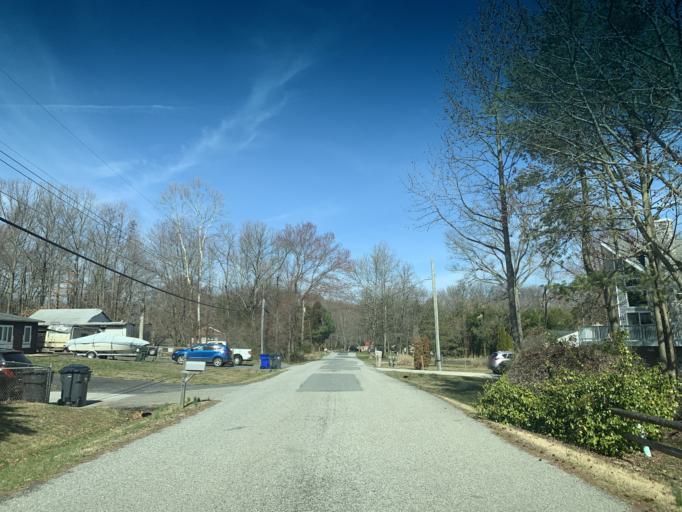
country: US
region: Maryland
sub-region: Cecil County
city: Charlestown
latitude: 39.5445
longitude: -76.0072
